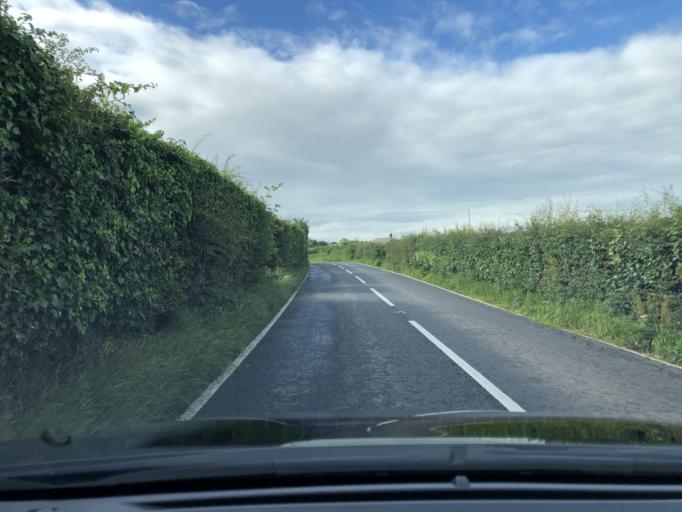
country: GB
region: Northern Ireland
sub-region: Down District
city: Dundrum
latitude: 54.2674
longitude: -5.7840
